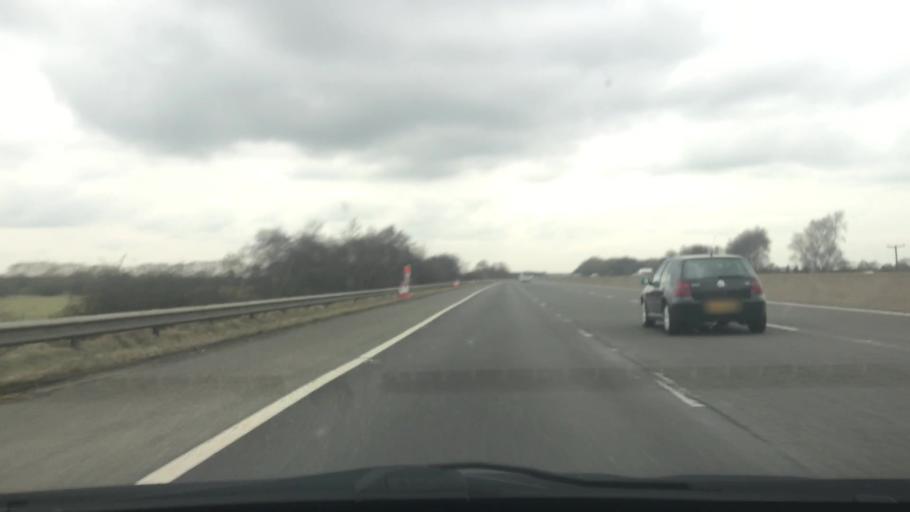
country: GB
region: England
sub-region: North Lincolnshire
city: Crowle
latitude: 53.5728
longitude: -0.9019
